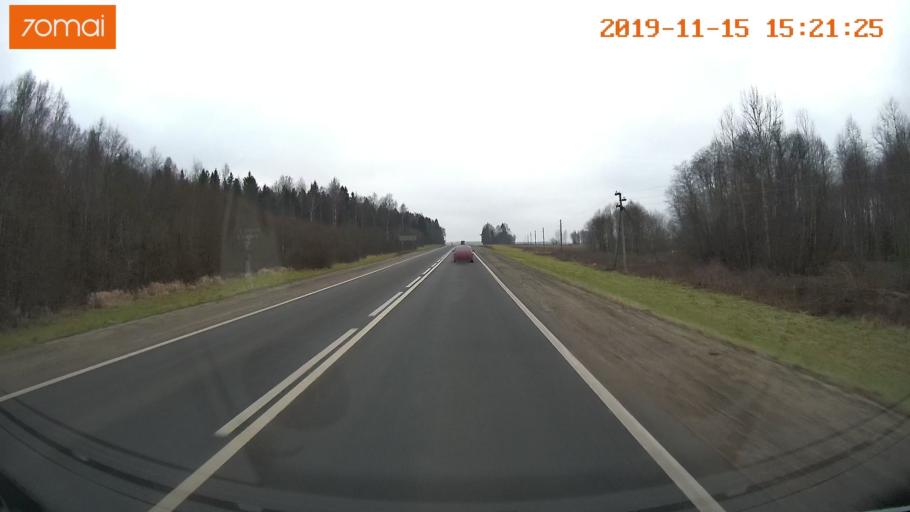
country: RU
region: Jaroslavl
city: Danilov
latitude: 58.2127
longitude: 40.1458
